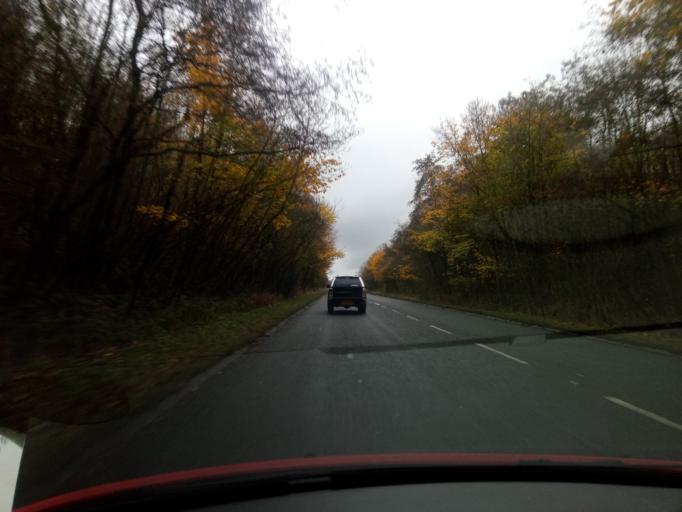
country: GB
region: England
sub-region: County Durham
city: High Etherley
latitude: 54.6636
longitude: -1.7726
